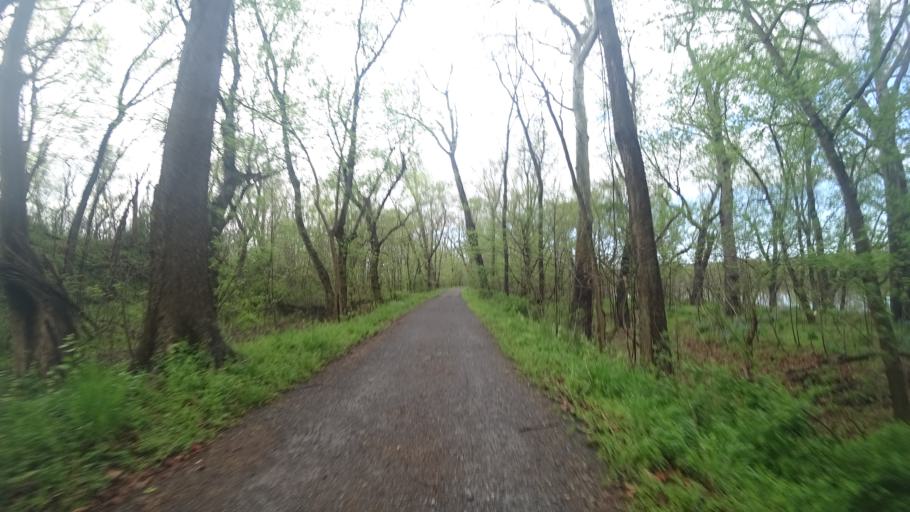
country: US
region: Virginia
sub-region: Loudoun County
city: Leesburg
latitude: 39.1344
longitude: -77.5144
